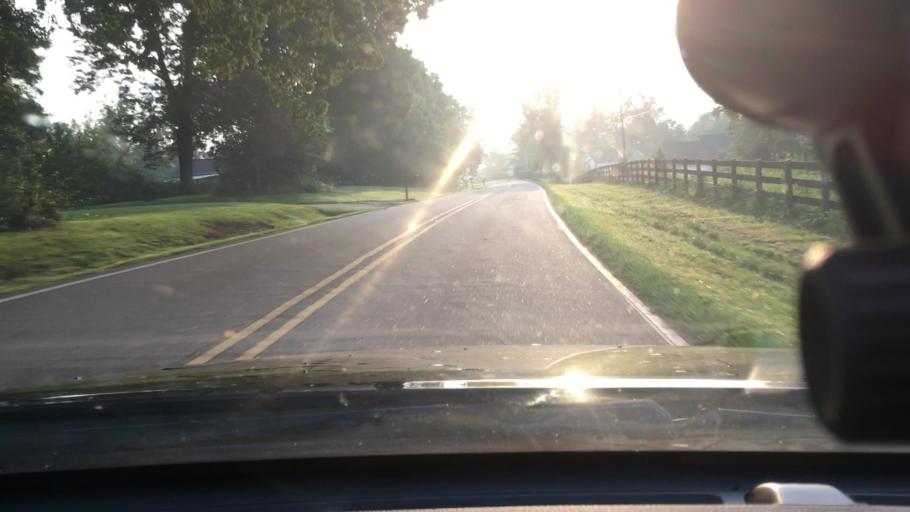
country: US
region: North Carolina
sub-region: Rutherford County
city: Rutherfordton
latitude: 35.3970
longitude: -81.9842
